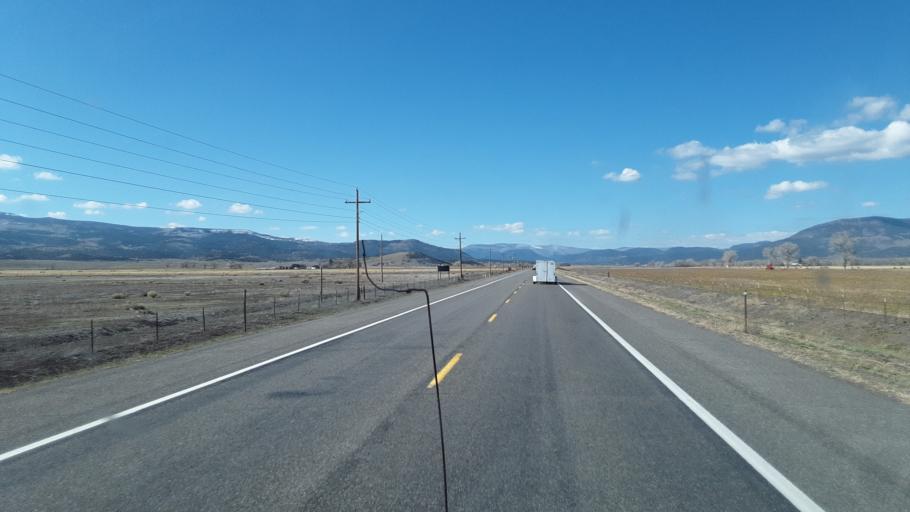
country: US
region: Colorado
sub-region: Rio Grande County
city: Del Norte
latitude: 37.6768
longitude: -106.4374
